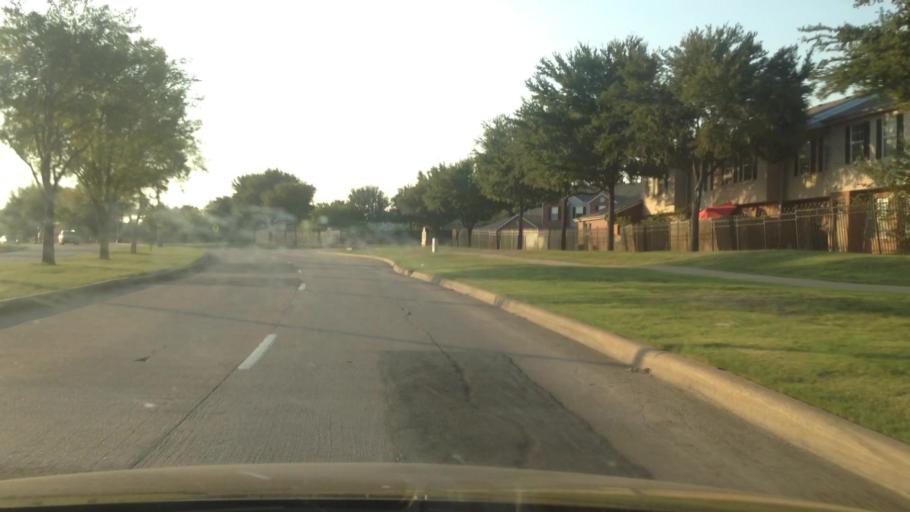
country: US
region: Texas
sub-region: Tarrant County
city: Dalworthington Gardens
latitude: 32.6474
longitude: -97.1257
